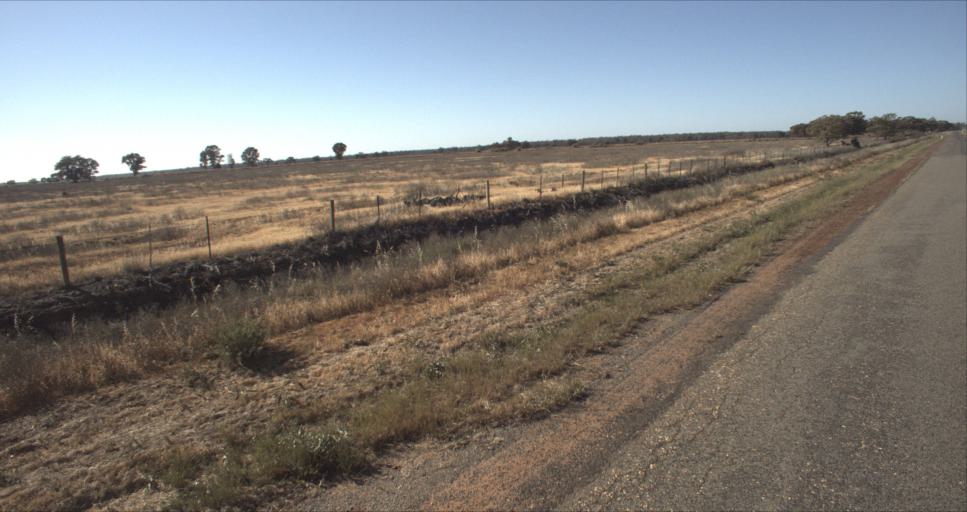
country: AU
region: New South Wales
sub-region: Leeton
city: Leeton
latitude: -34.5844
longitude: 146.2609
